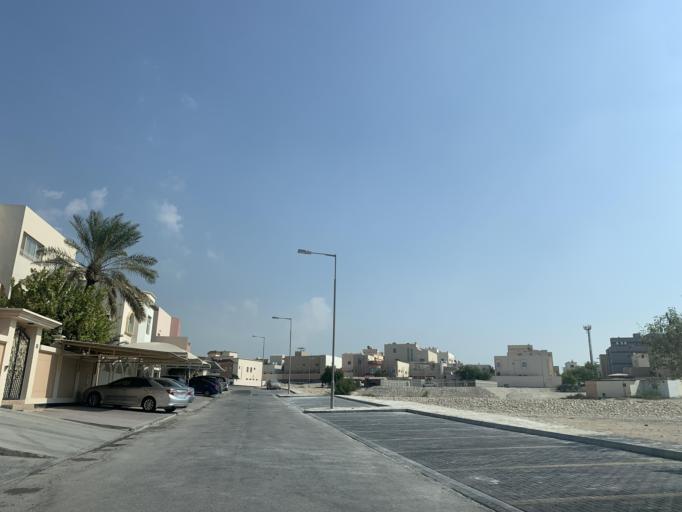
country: BH
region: Central Governorate
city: Madinat Hamad
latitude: 26.1133
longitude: 50.5004
